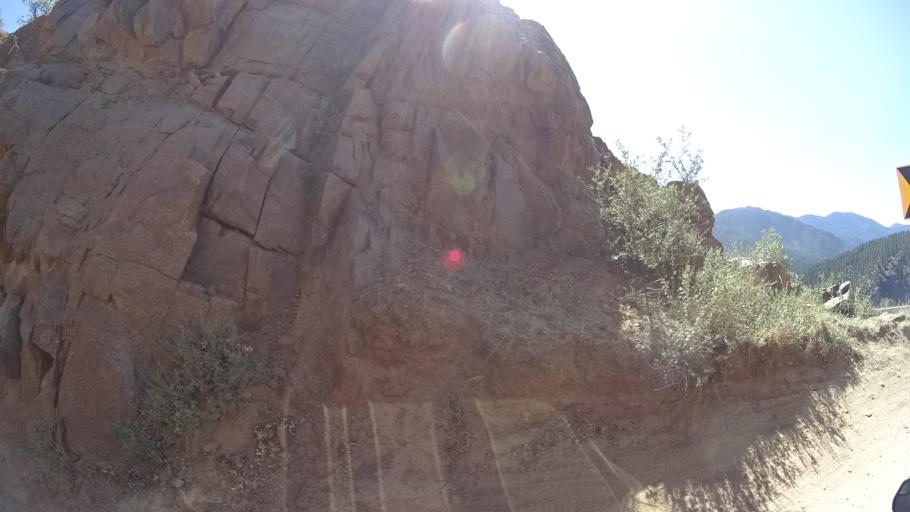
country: US
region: Colorado
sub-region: El Paso County
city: Colorado Springs
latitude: 38.7950
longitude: -104.8757
